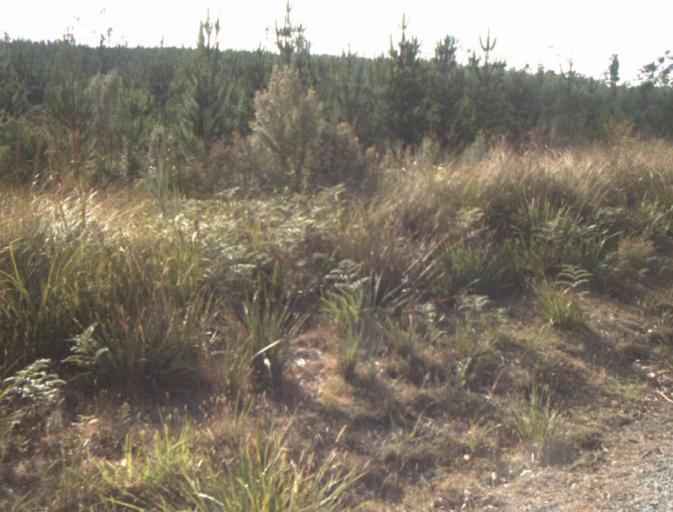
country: AU
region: Tasmania
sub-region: Dorset
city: Bridport
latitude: -41.1421
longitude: 147.2284
